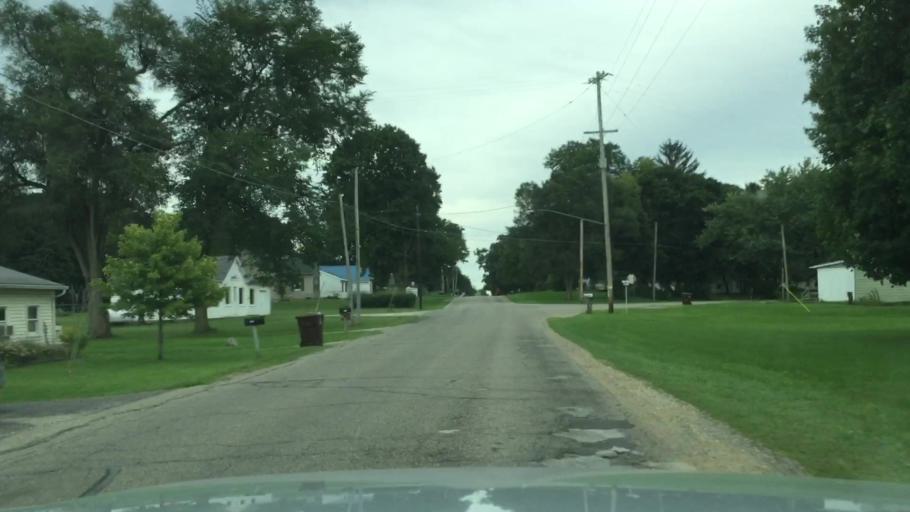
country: US
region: Michigan
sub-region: Shiawassee County
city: Durand
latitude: 42.8803
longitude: -84.0656
